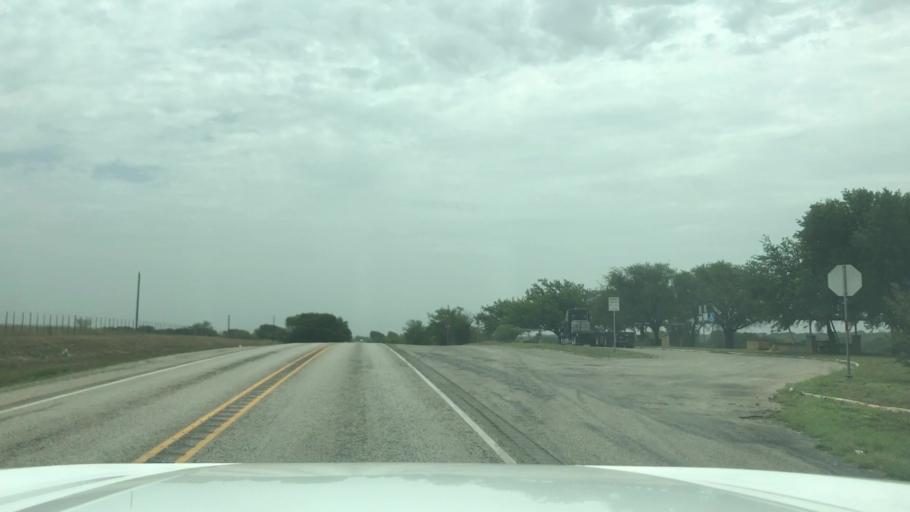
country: US
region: Texas
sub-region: Hamilton County
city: Hico
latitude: 32.0469
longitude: -98.1490
